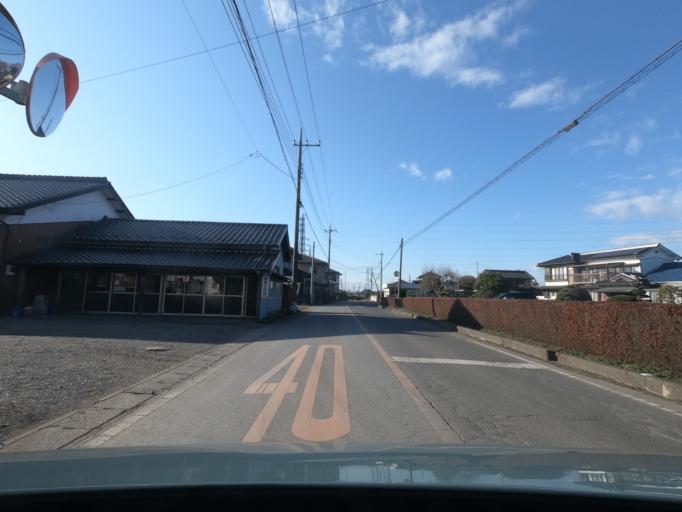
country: JP
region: Ibaraki
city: Koga
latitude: 36.2394
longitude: 139.7474
